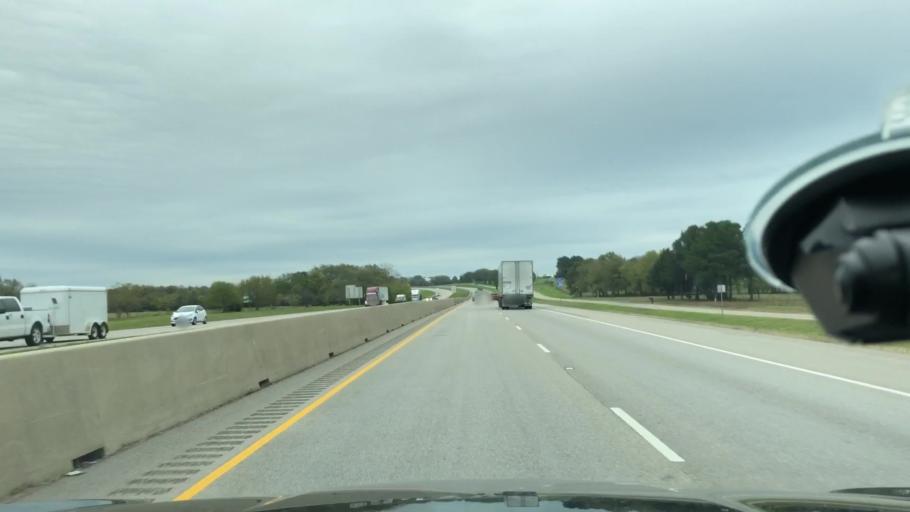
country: US
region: Texas
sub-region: Franklin County
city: Mount Vernon
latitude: 33.1614
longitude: -95.2102
